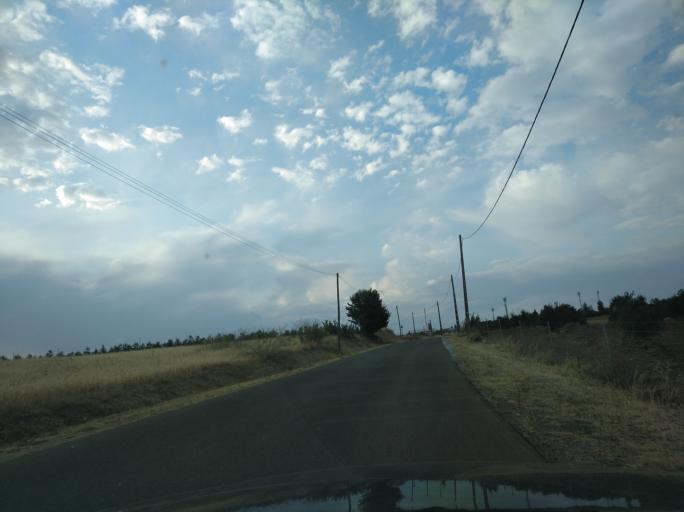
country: PT
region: Portalegre
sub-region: Campo Maior
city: Campo Maior
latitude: 39.0067
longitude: -7.0612
